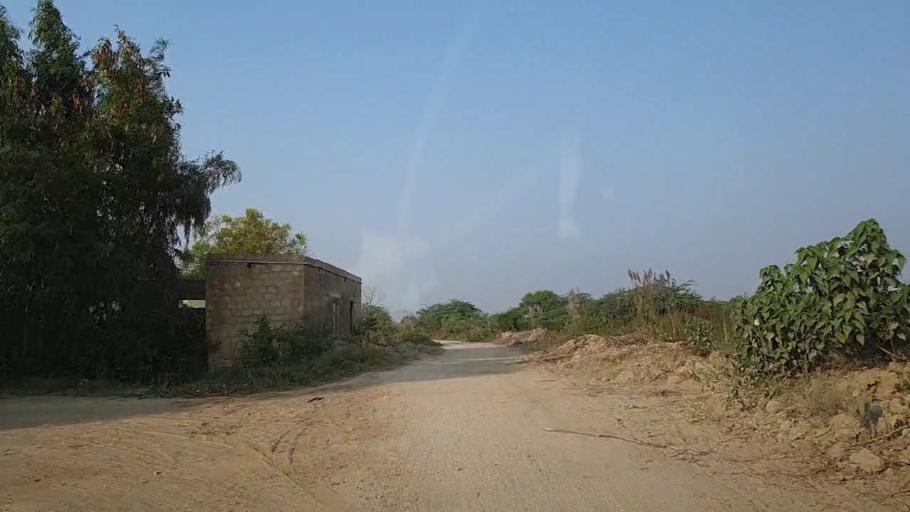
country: PK
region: Sindh
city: Thatta
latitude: 24.6723
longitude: 67.7830
